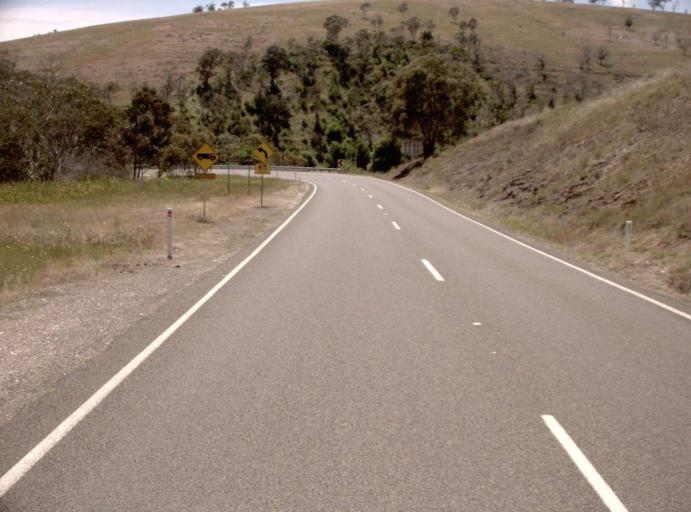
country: AU
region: Victoria
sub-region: Alpine
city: Mount Beauty
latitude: -37.1130
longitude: 147.5762
